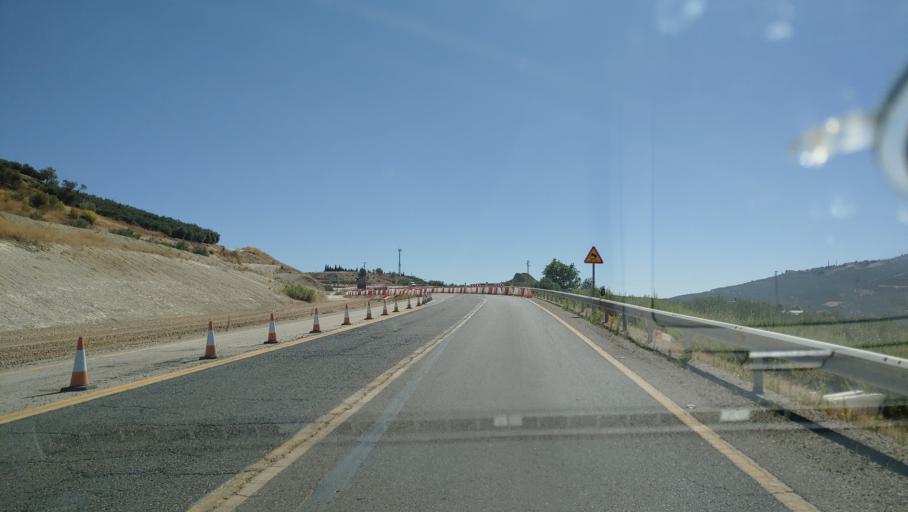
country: ES
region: Andalusia
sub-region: Provincia de Jaen
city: Villanueva del Arzobispo
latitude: 38.1742
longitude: -2.9902
